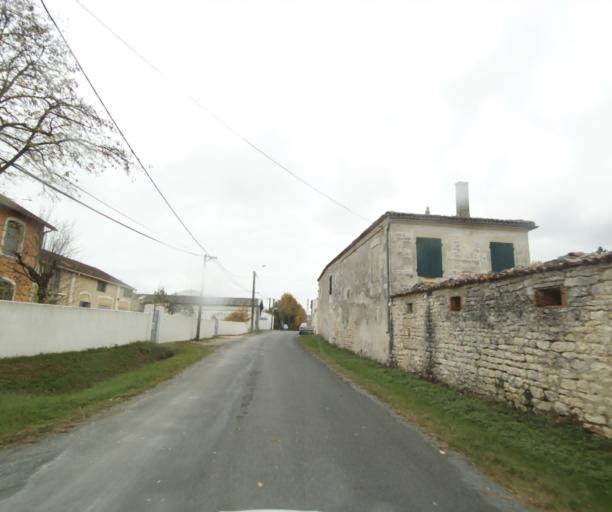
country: FR
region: Poitou-Charentes
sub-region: Departement de la Charente-Maritime
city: Saintes
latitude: 45.7631
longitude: -0.6262
